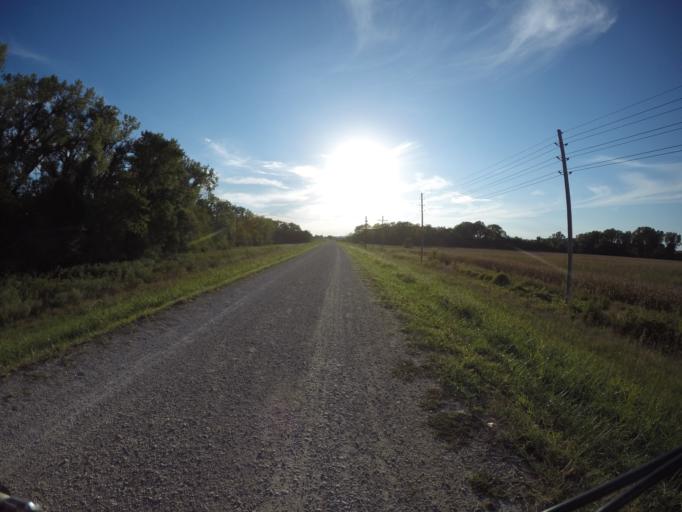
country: US
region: Kansas
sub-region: Riley County
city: Manhattan
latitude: 39.1844
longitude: -96.5442
